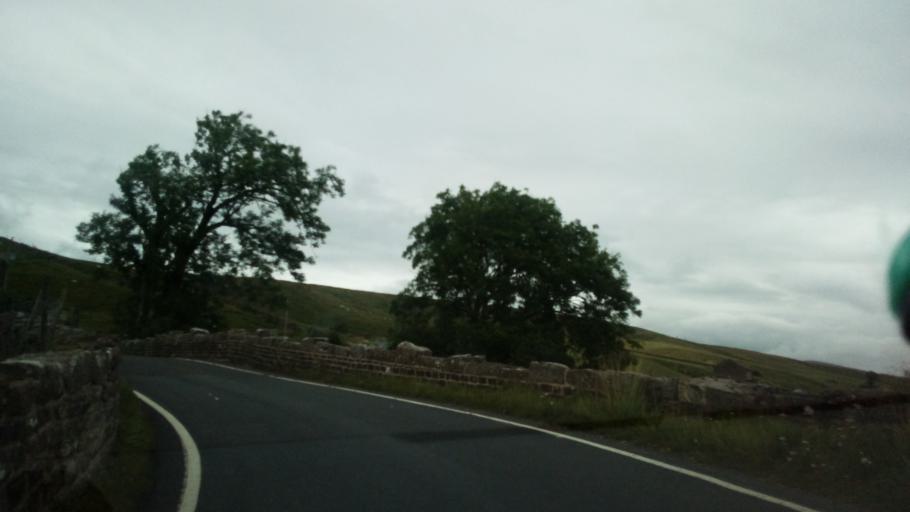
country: GB
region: England
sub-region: County Durham
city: Holwick
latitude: 54.5816
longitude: -2.2062
